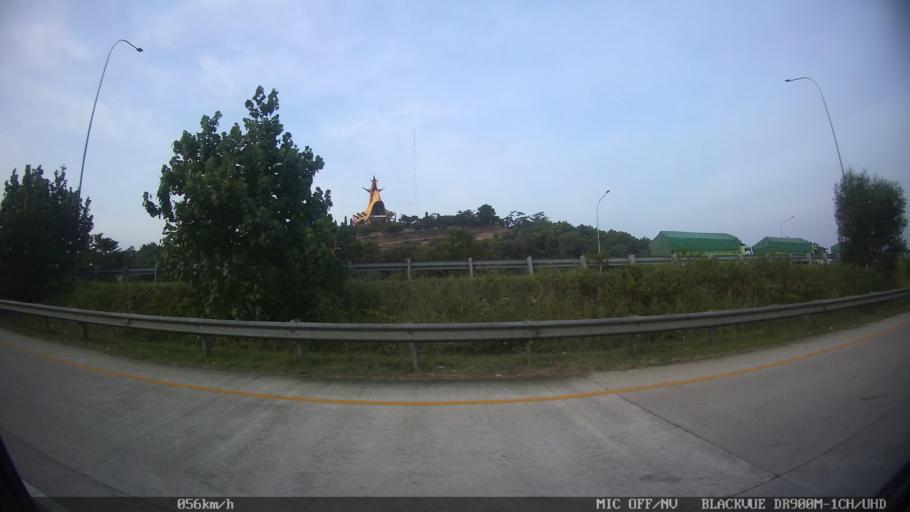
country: ID
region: Lampung
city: Penengahan
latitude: -5.8678
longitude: 105.7491
